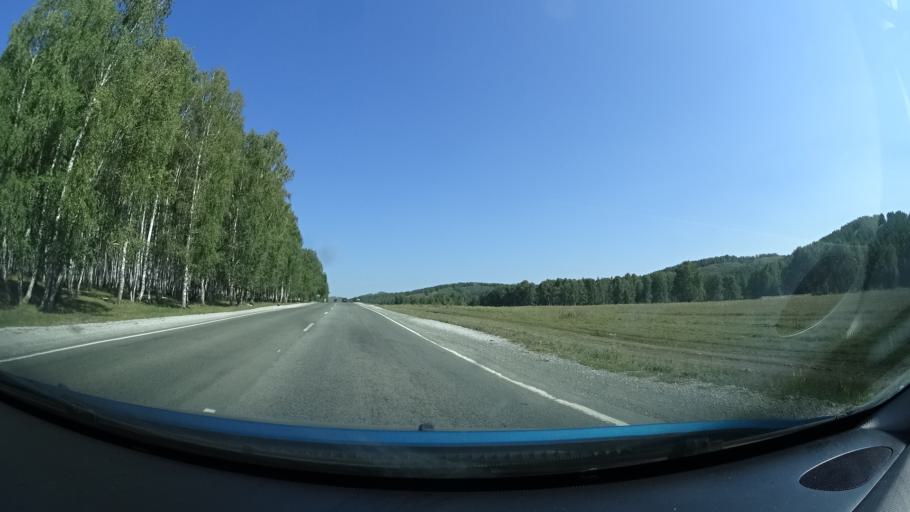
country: RU
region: Bashkortostan
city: Abzakovo
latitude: 53.8411
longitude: 58.5815
